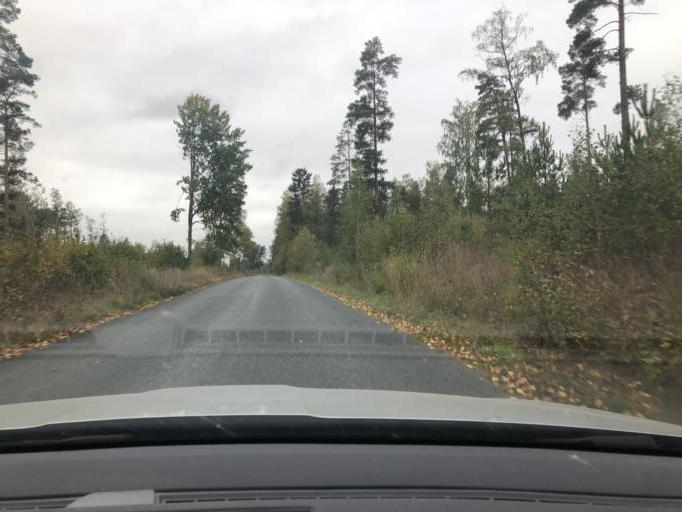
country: SE
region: Vaestmanland
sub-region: Kungsors Kommun
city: Kungsoer
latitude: 59.2294
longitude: 16.0960
